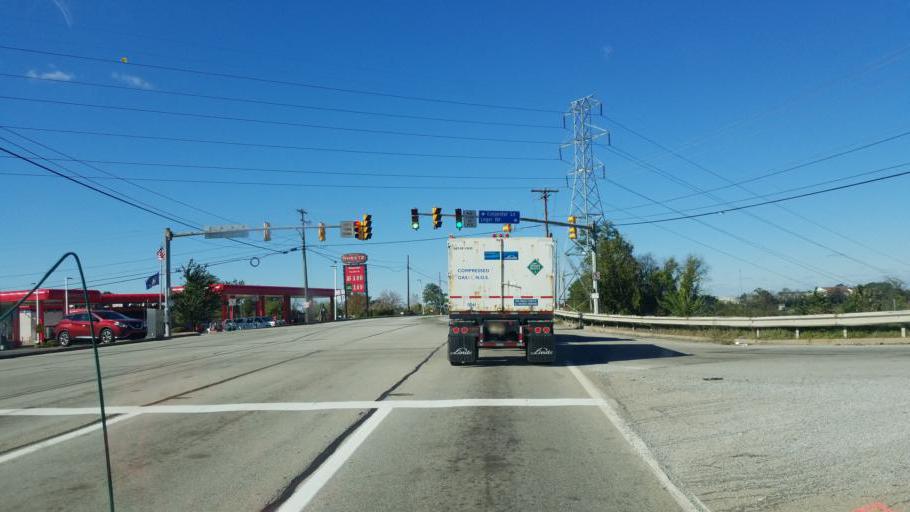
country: US
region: Pennsylvania
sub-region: Westmoreland County
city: Trafford
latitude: 40.3453
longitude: -79.7642
